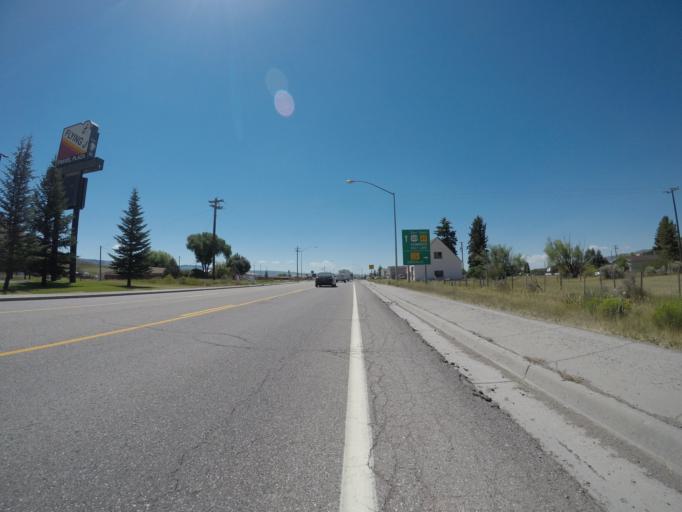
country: US
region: Idaho
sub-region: Bear Lake County
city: Montpelier
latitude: 42.0864
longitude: -110.9488
